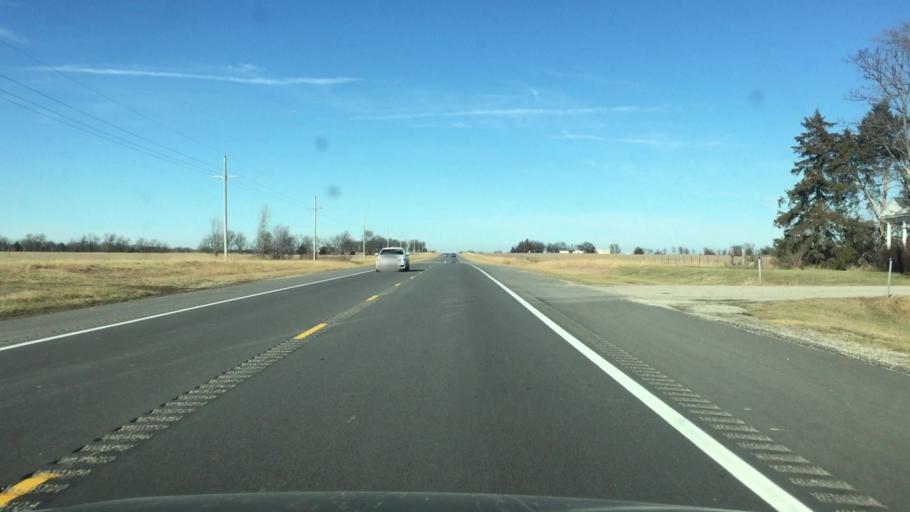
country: US
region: Kansas
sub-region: Franklin County
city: Ottawa
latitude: 38.5249
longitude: -95.2676
